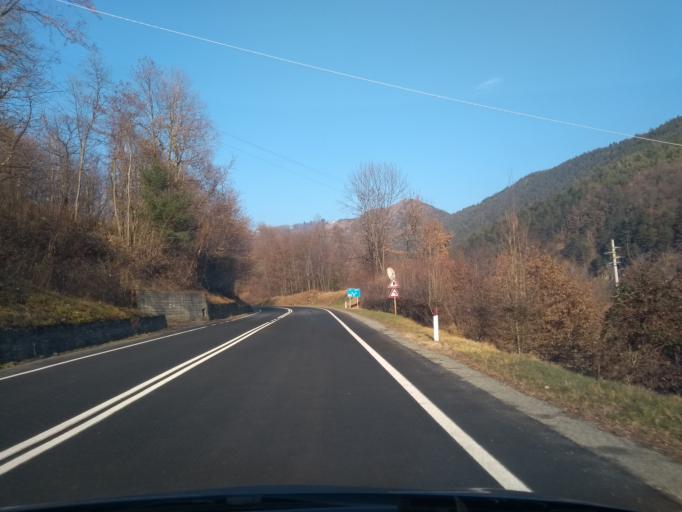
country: IT
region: Piedmont
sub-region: Provincia di Torino
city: Germagnano
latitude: 45.2593
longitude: 7.4587
